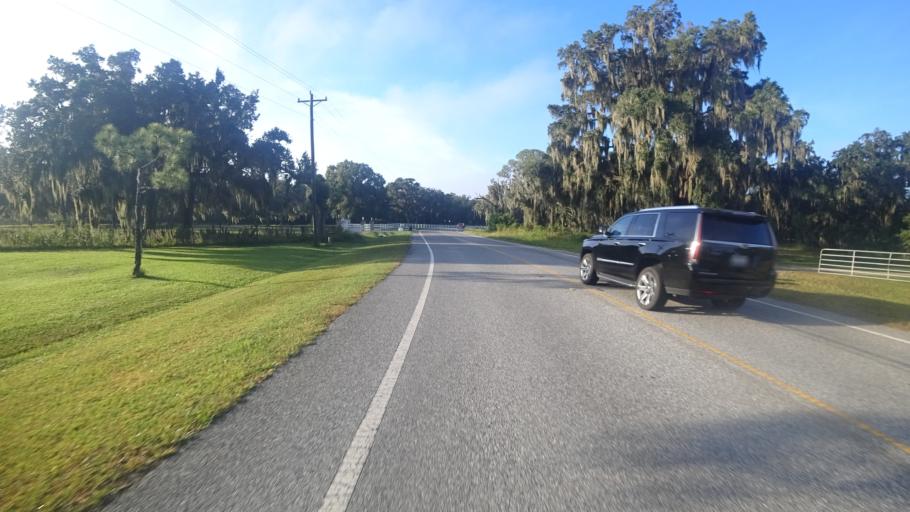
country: US
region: Florida
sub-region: Manatee County
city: Ellenton
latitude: 27.5477
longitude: -82.4478
